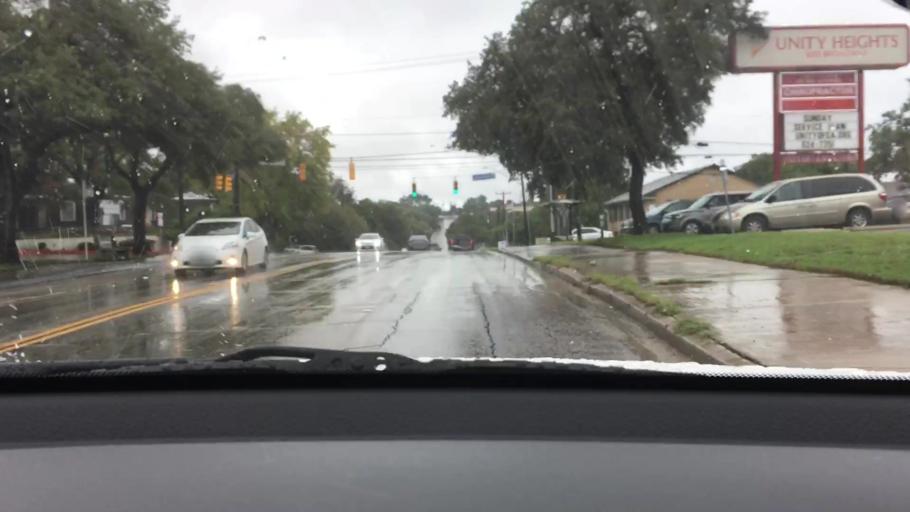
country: US
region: Texas
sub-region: Bexar County
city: Alamo Heights
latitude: 29.5103
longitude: -98.4662
